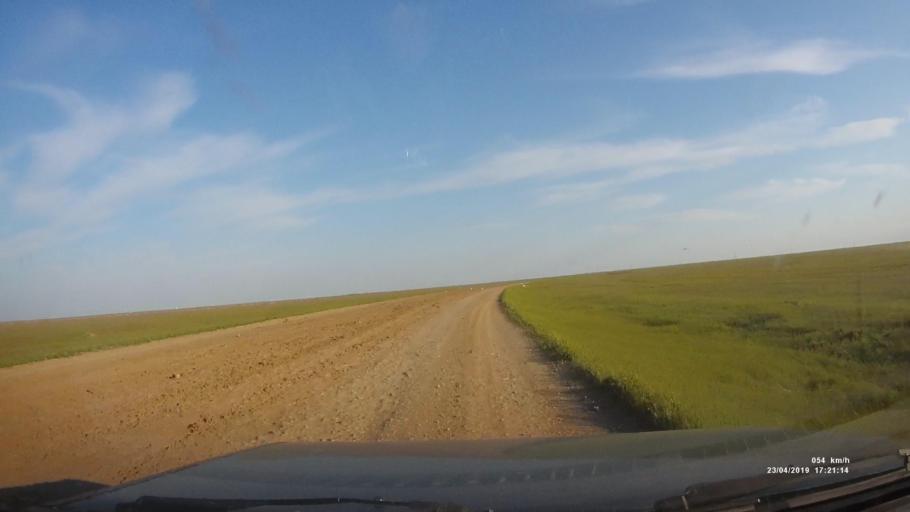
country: RU
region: Kalmykiya
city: Priyutnoye
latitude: 46.1776
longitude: 43.5045
